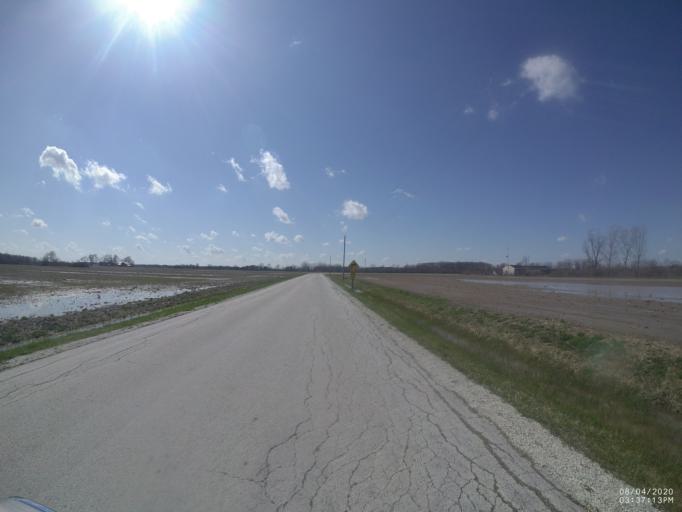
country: US
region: Ohio
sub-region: Sandusky County
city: Stony Prairie
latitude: 41.2566
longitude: -83.2557
